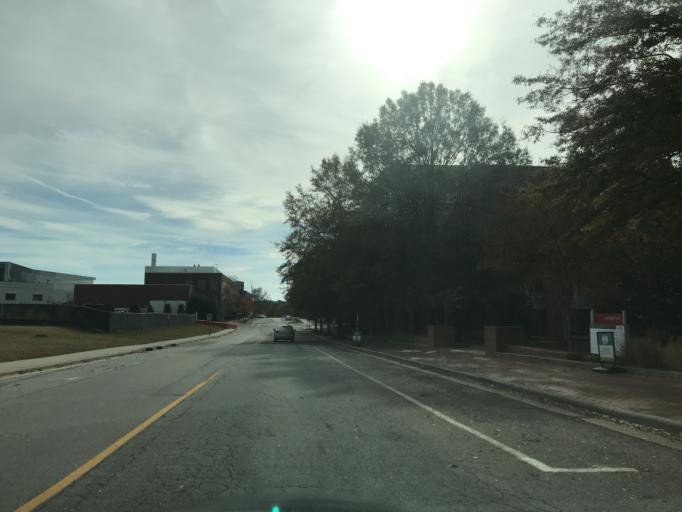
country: US
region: North Carolina
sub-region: Wake County
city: West Raleigh
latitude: 35.7726
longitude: -78.6773
